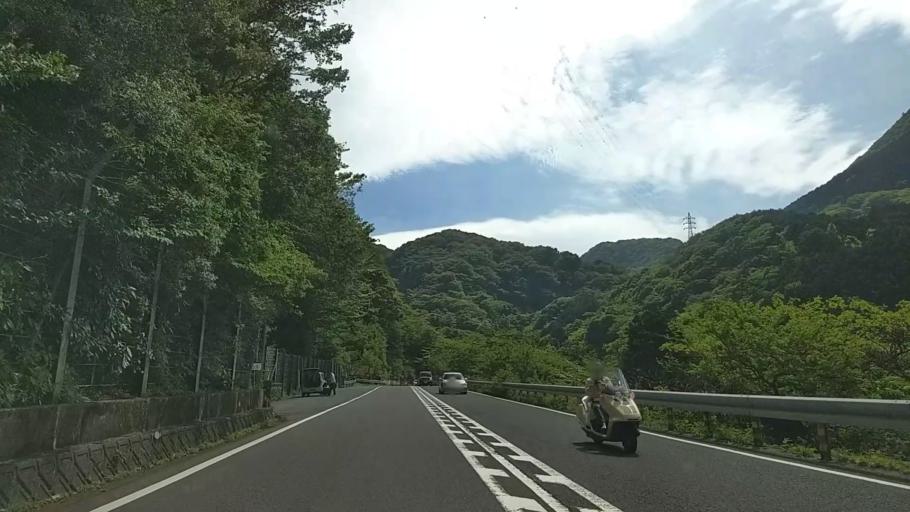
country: JP
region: Kanagawa
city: Hakone
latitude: 35.2108
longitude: 139.0641
